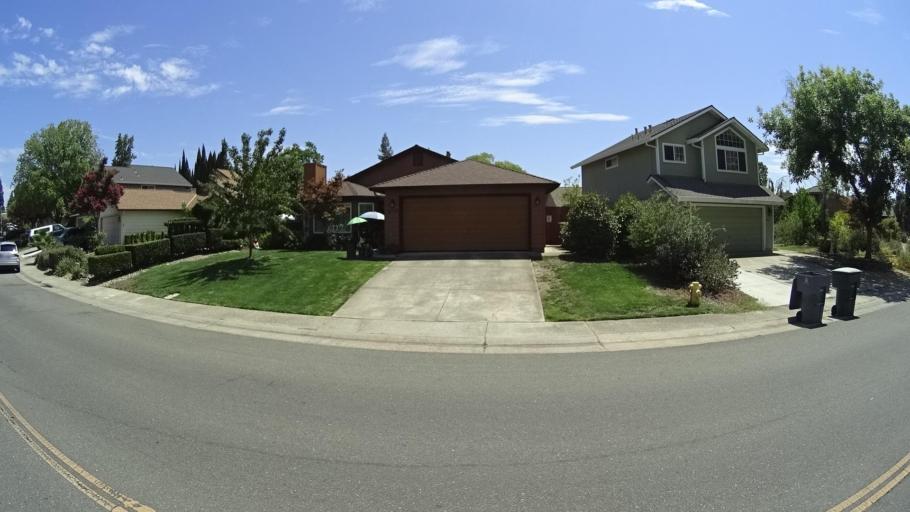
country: US
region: California
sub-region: Placer County
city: Rocklin
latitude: 38.8040
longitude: -121.2621
